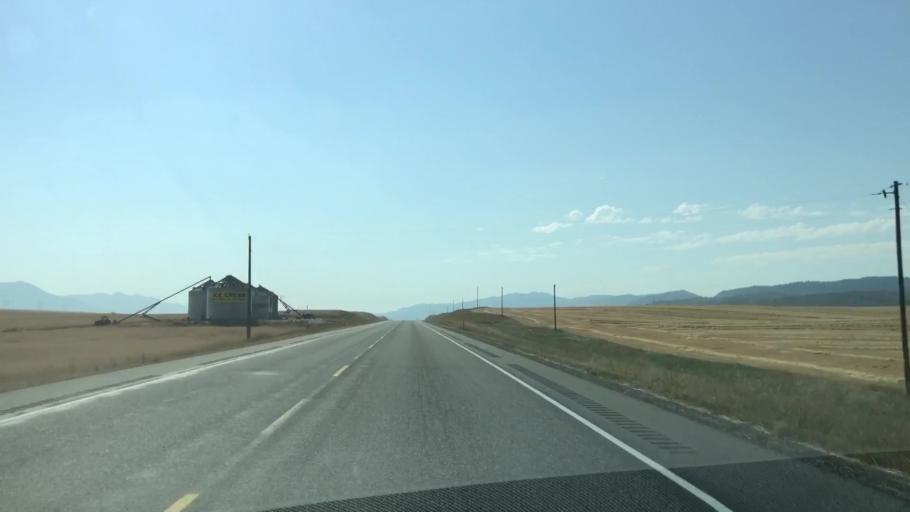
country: US
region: Idaho
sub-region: Teton County
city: Victor
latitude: 43.5169
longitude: -111.4865
